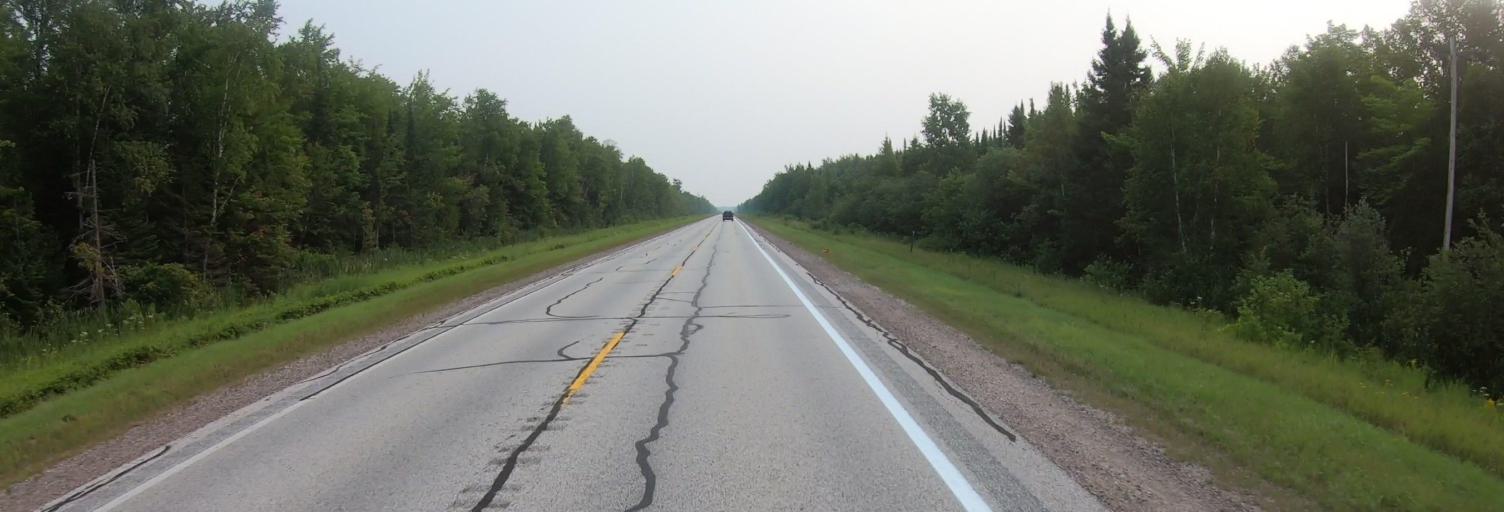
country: US
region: Michigan
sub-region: Luce County
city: Newberry
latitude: 46.5235
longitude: -85.0725
